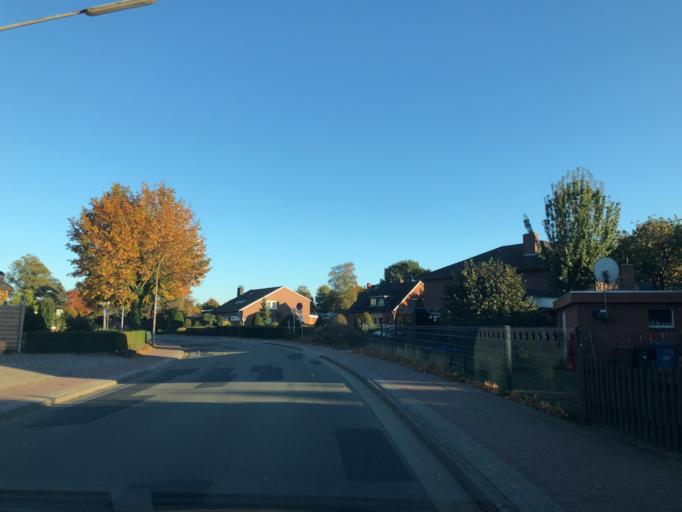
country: DE
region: Lower Saxony
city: Friesoythe
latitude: 53.0248
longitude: 7.8492
